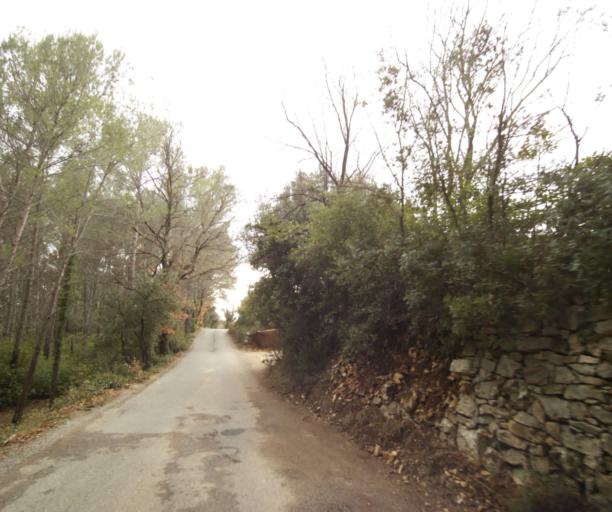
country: FR
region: Provence-Alpes-Cote d'Azur
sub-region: Departement du Var
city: Trans-en-Provence
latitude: 43.5129
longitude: 6.4950
